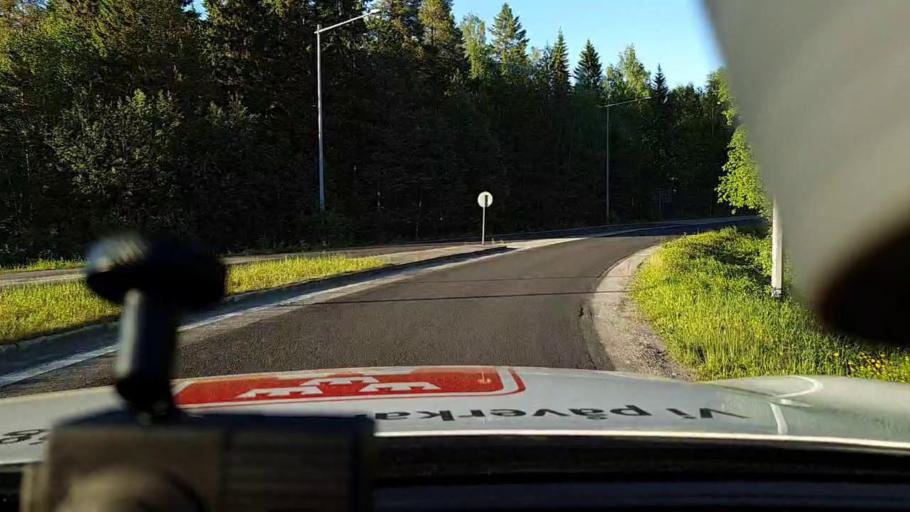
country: SE
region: Norrbotten
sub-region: Lulea Kommun
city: Lulea
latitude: 65.6088
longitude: 22.1836
